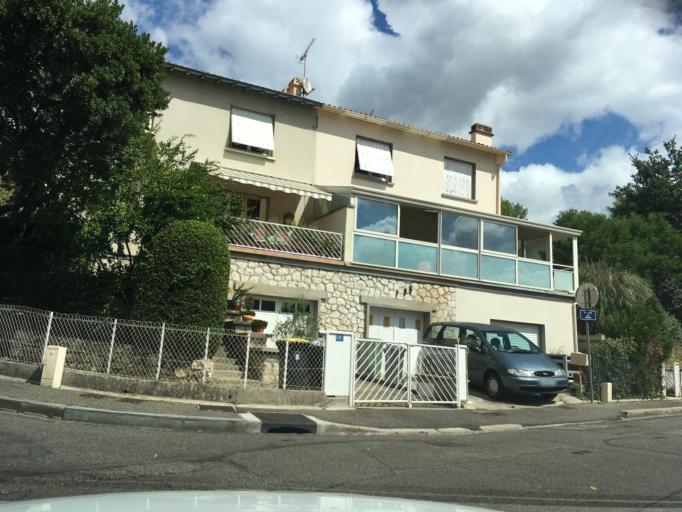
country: FR
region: Aquitaine
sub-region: Departement du Lot-et-Garonne
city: Agen
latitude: 44.2110
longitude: 0.6385
